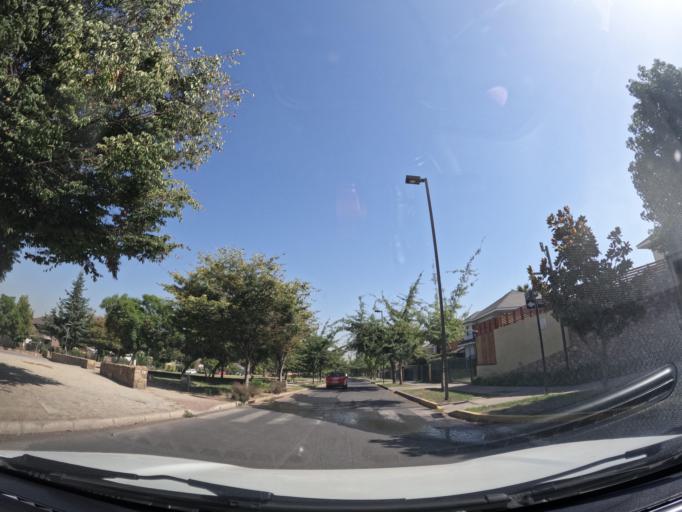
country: CL
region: Santiago Metropolitan
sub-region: Provincia de Santiago
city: Villa Presidente Frei, Nunoa, Santiago, Chile
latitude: -33.4955
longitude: -70.5554
